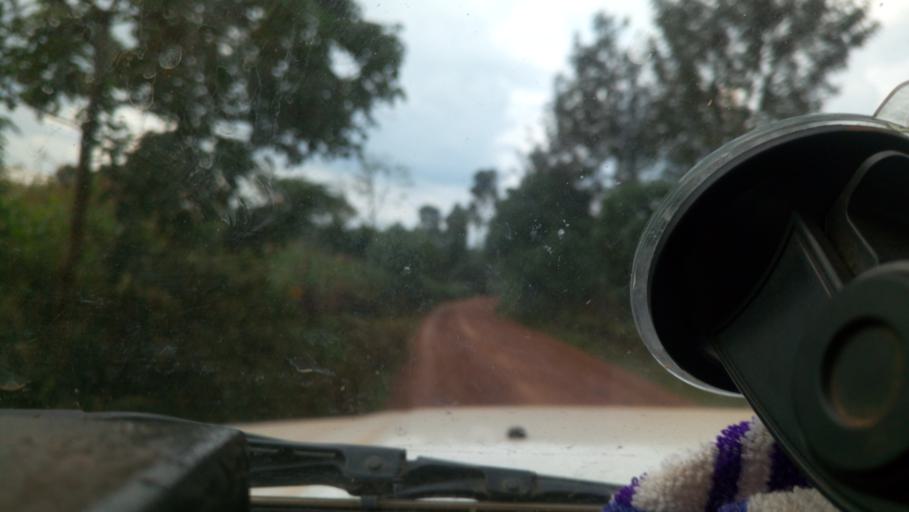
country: KE
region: Kericho
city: Litein
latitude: -0.5969
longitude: 35.1213
